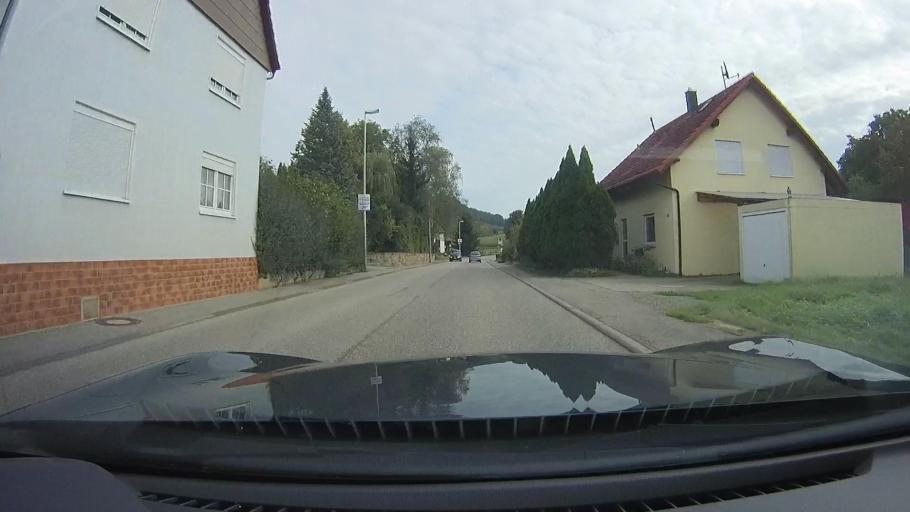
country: DE
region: Baden-Wuerttemberg
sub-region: Regierungsbezirk Stuttgart
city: Abstatt
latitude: 49.0869
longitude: 9.2993
